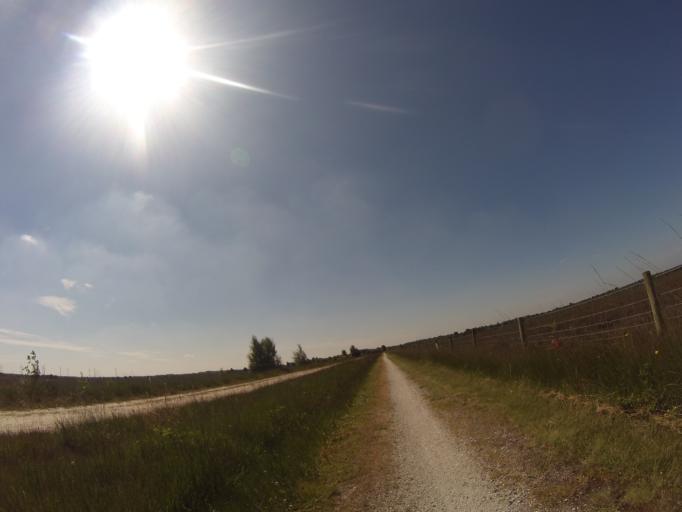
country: NL
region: Drenthe
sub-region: Gemeente Emmen
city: Klazienaveen
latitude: 52.6821
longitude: 7.0234
